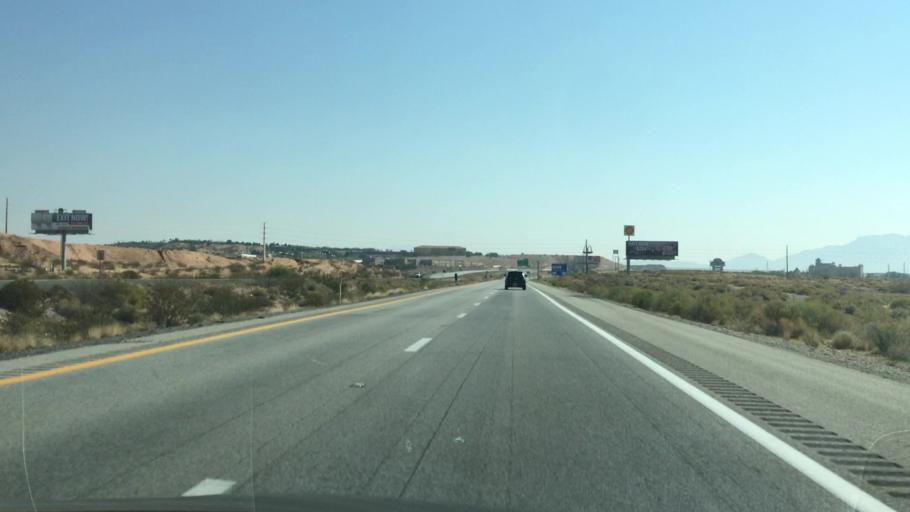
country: US
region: Nevada
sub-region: Clark County
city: Bunkerville
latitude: 36.7973
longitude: -114.1162
